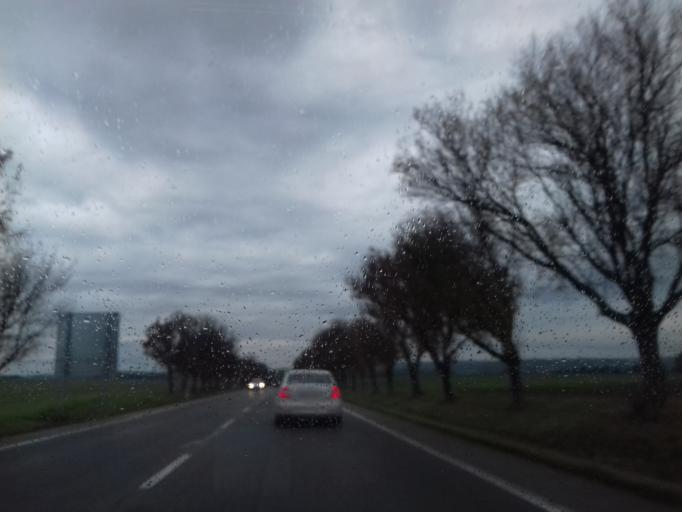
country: CZ
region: Pardubicky
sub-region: Okres Pardubice
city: Vysoke Myto
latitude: 49.9871
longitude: 16.1119
